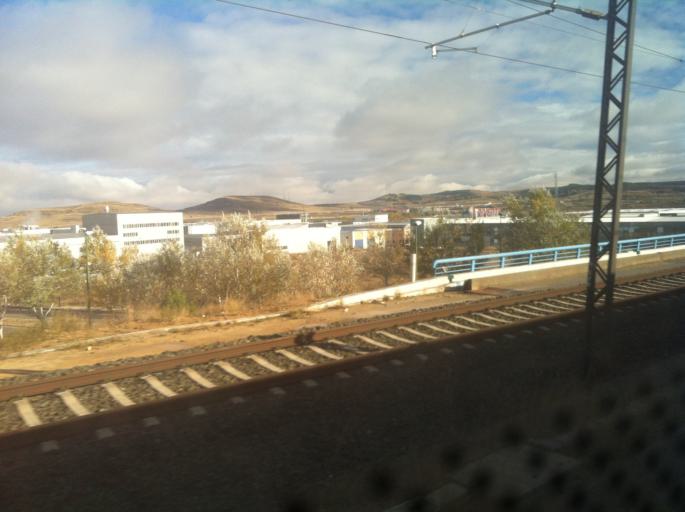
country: ES
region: Castille and Leon
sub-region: Provincia de Burgos
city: Sotragero
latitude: 42.3684
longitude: -3.7172
